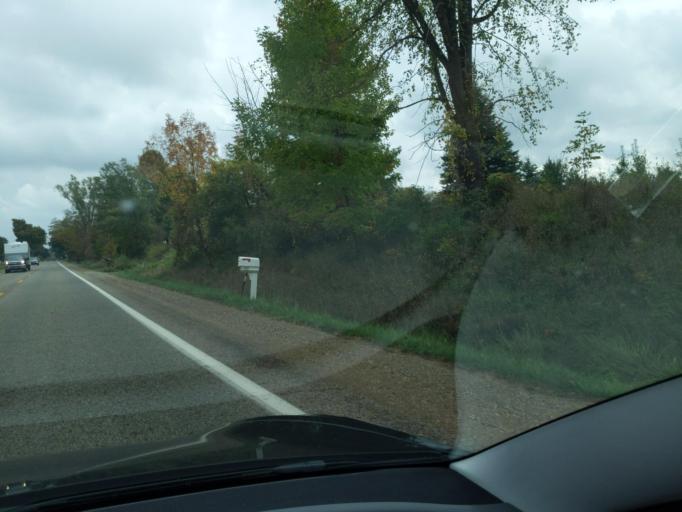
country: US
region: Michigan
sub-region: Eaton County
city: Potterville
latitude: 42.5481
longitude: -84.7494
